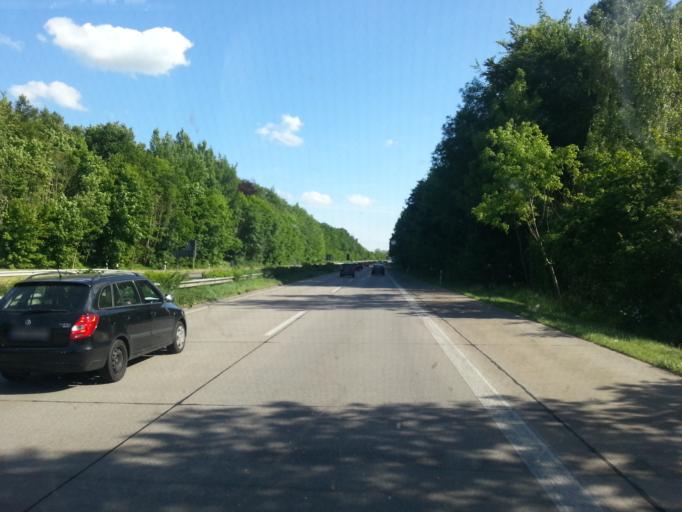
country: DE
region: Schleswig-Holstein
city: Scharbeutz
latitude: 54.0331
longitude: 10.7296
